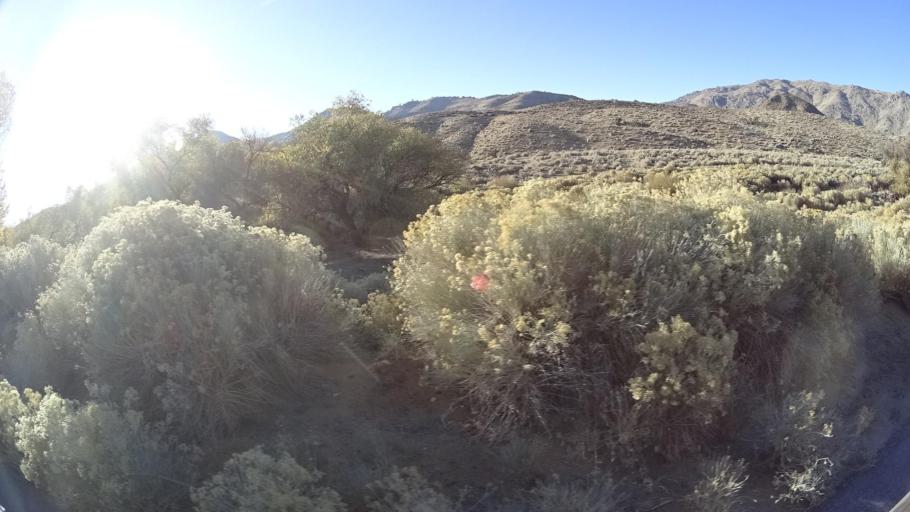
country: US
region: California
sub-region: Kern County
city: Weldon
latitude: 35.4677
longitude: -118.2112
